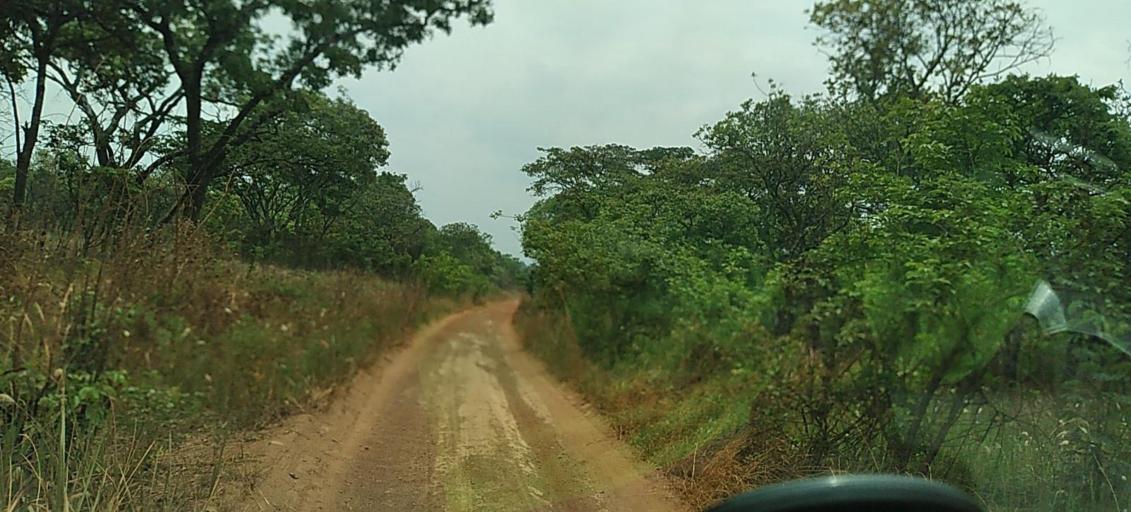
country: ZM
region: North-Western
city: Kansanshi
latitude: -12.0349
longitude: 26.3183
